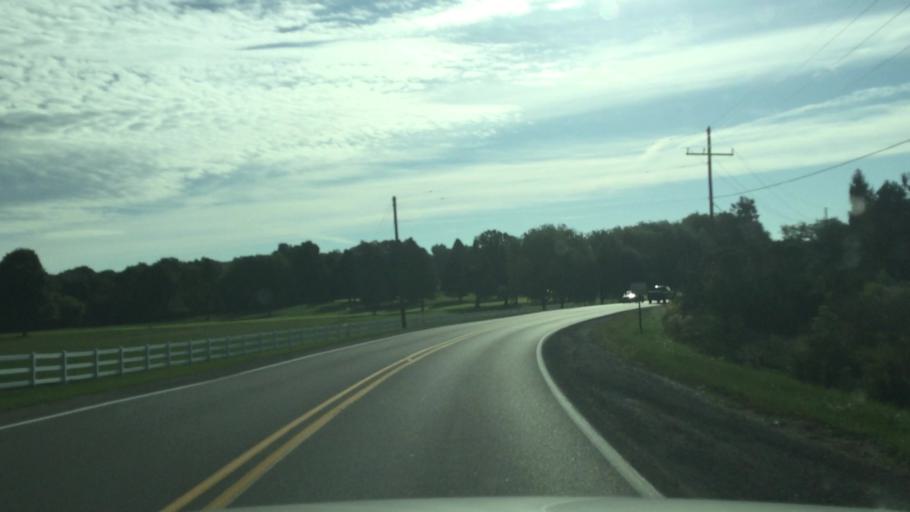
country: US
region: Michigan
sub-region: Livingston County
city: Howell
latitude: 42.6047
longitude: -83.8940
